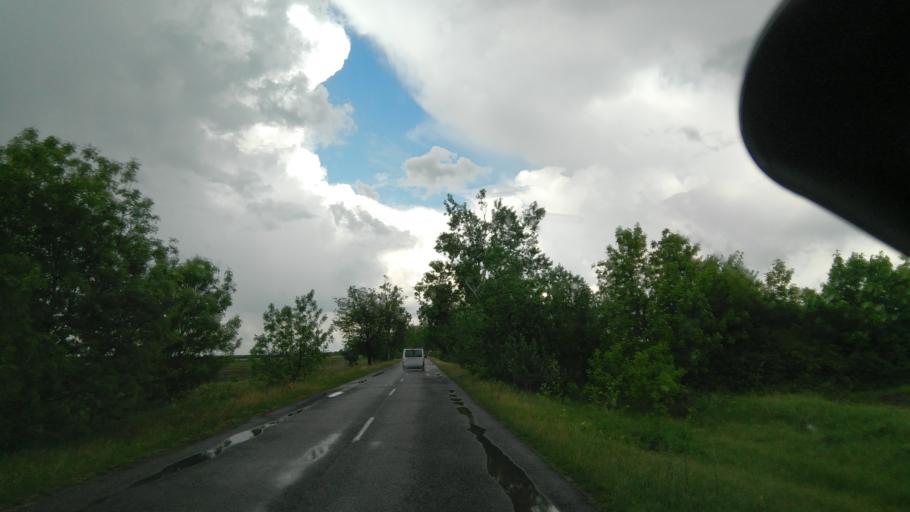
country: HU
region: Bekes
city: Fuzesgyarmat
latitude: 47.1417
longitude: 21.1457
